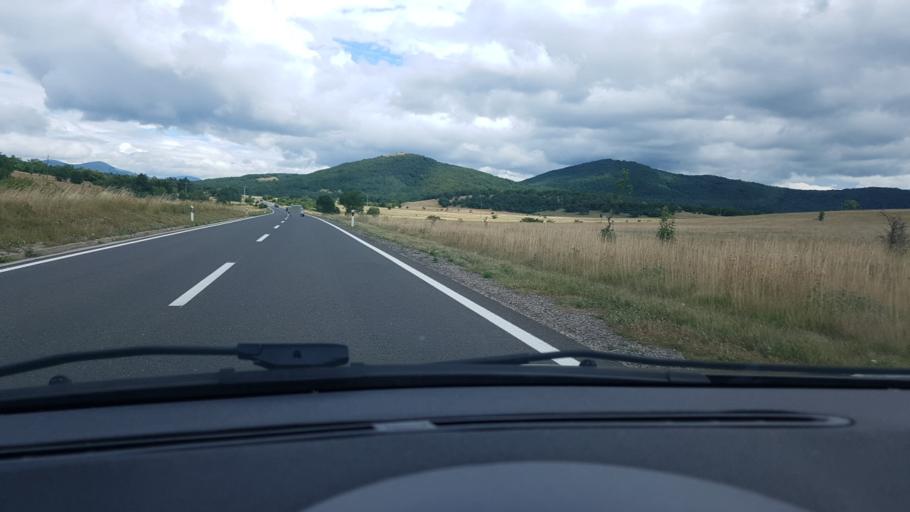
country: HR
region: Zadarska
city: Gracac
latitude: 44.4674
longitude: 15.7989
